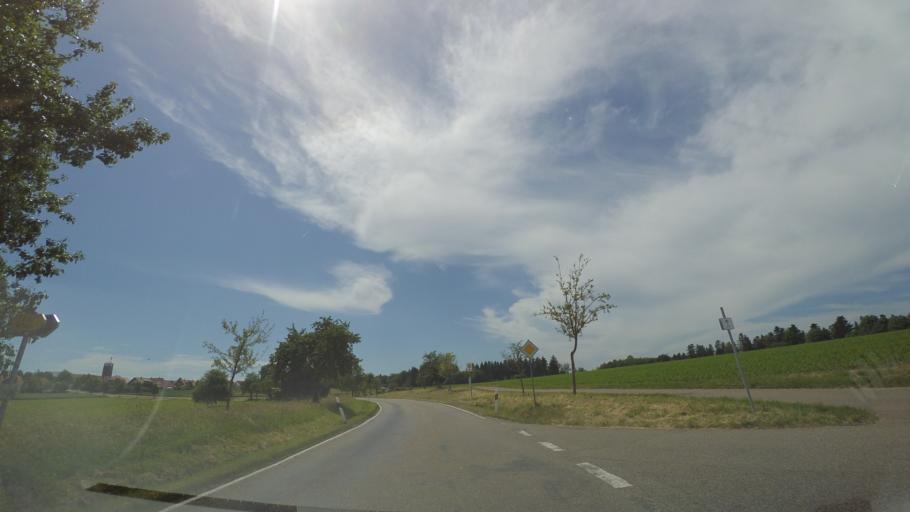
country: DE
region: Baden-Wuerttemberg
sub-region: Regierungsbezirk Stuttgart
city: Kaisersbach
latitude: 48.9357
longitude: 9.6414
